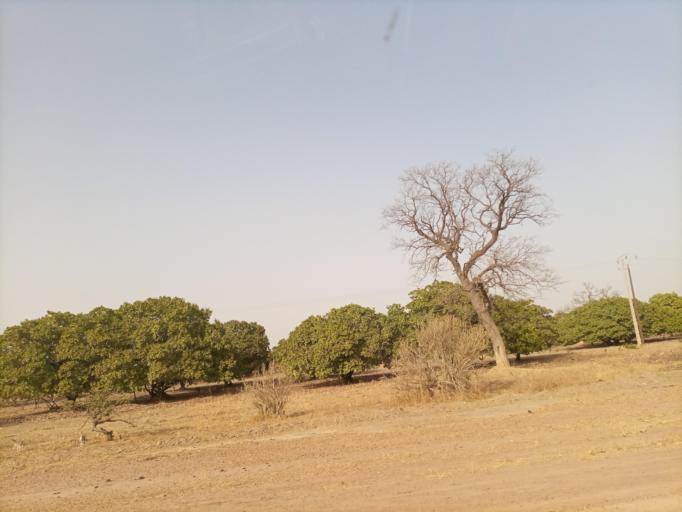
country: SN
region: Fatick
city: Passi
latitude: 14.0206
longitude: -16.2966
